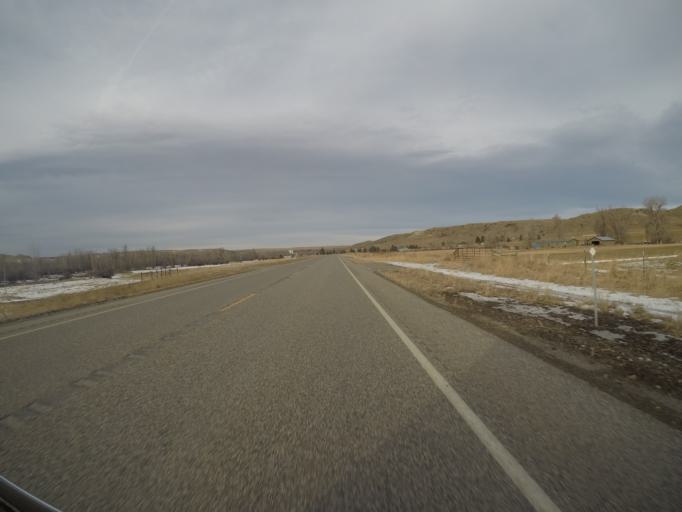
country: US
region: Montana
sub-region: Stillwater County
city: Absarokee
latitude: 45.4743
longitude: -109.4487
